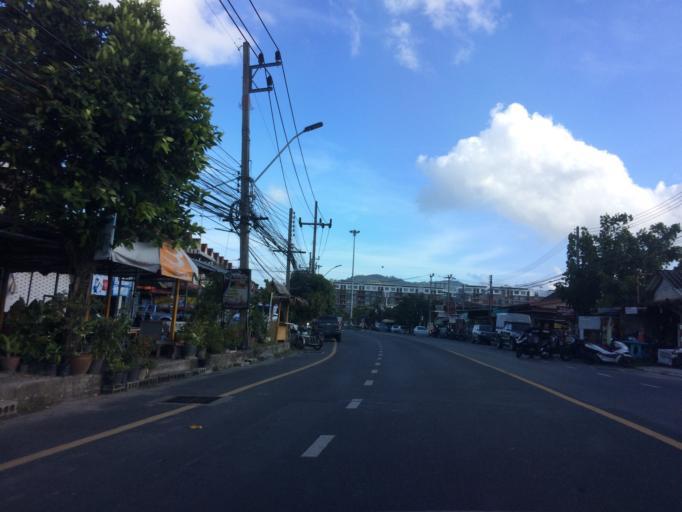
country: TH
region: Phuket
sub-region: Amphoe Kathu
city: Kathu
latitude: 7.9134
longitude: 98.3467
